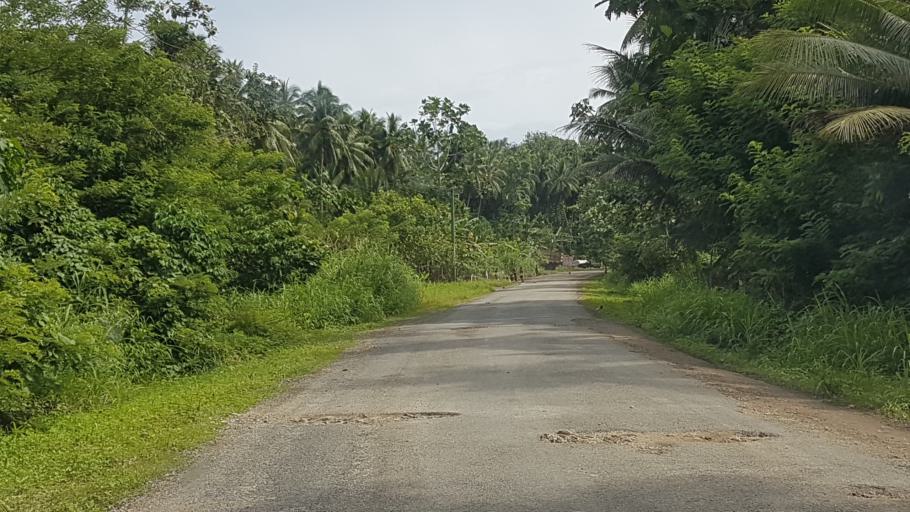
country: PG
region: Madang
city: Madang
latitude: -4.8794
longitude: 145.7933
